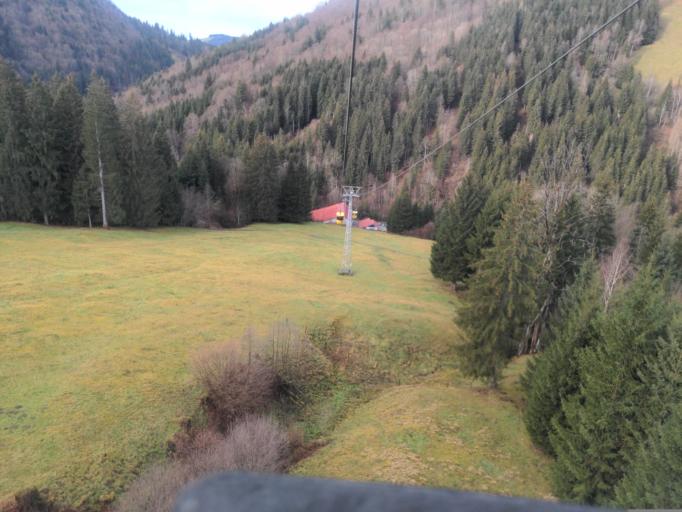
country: DE
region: Bavaria
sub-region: Swabia
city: Balderschwang
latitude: 47.5073
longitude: 10.0601
